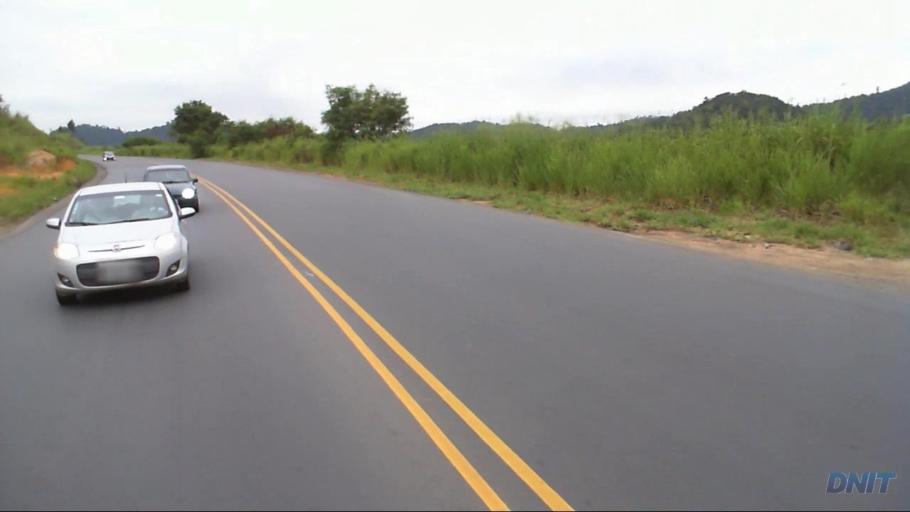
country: BR
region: Minas Gerais
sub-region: Coronel Fabriciano
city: Coronel Fabriciano
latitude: -19.5351
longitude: -42.5901
